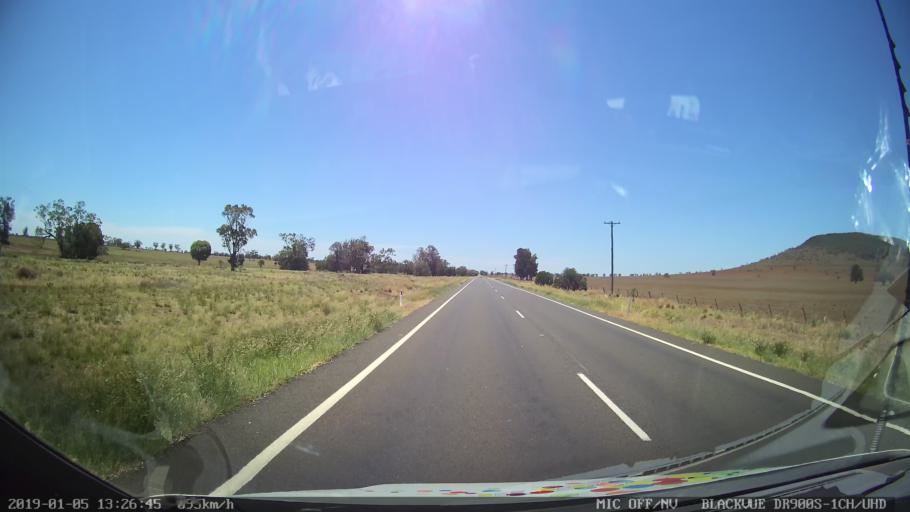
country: AU
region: New South Wales
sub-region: Gunnedah
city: Gunnedah
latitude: -31.0503
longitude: 150.0200
